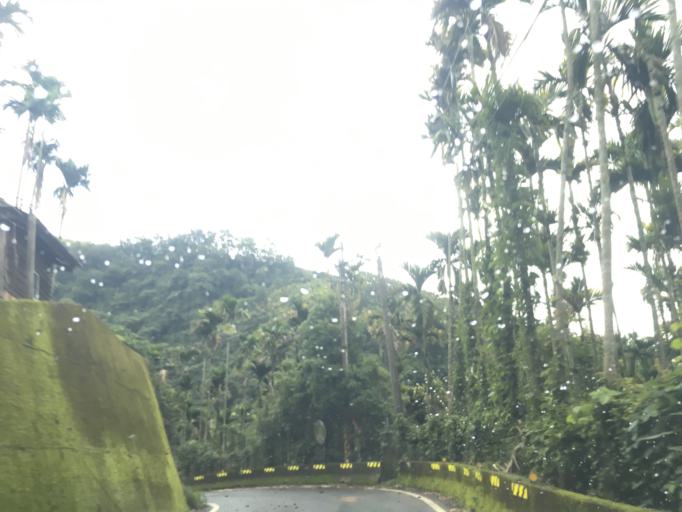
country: TW
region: Taiwan
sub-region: Yunlin
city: Douliu
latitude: 23.5642
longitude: 120.6158
